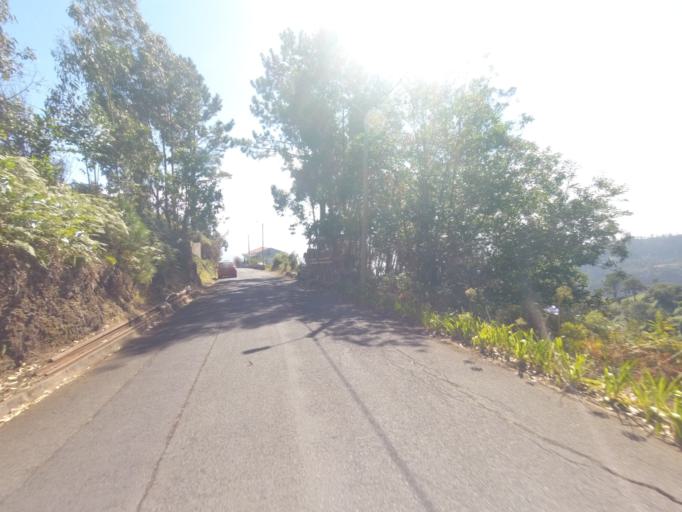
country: PT
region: Madeira
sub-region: Ribeira Brava
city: Campanario
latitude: 32.6960
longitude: -17.0299
